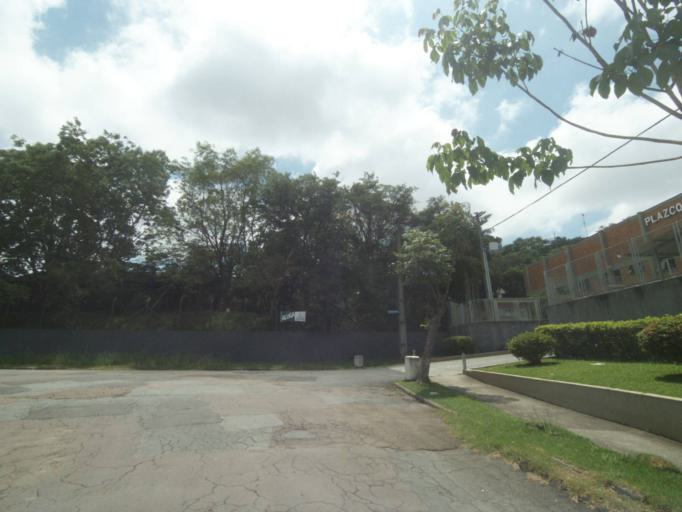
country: BR
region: Parana
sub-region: Curitiba
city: Curitiba
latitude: -25.5146
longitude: -49.3161
